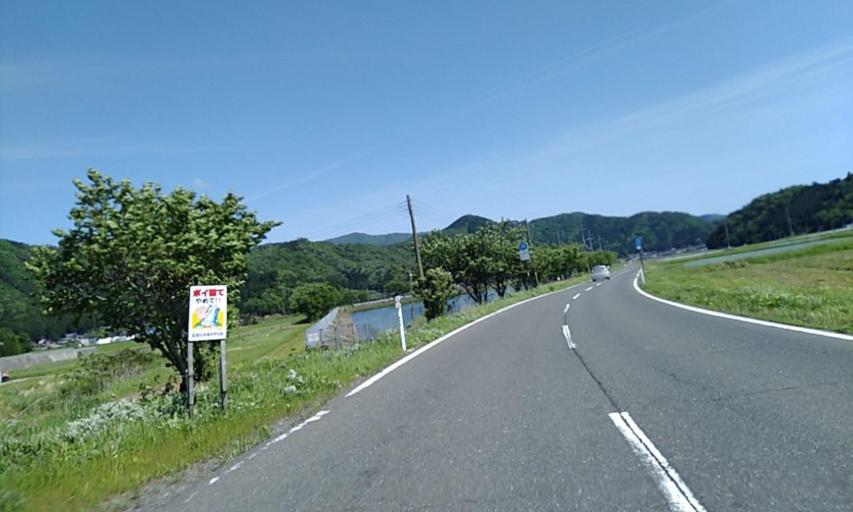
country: JP
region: Fukui
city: Obama
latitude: 35.5246
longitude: 135.8579
